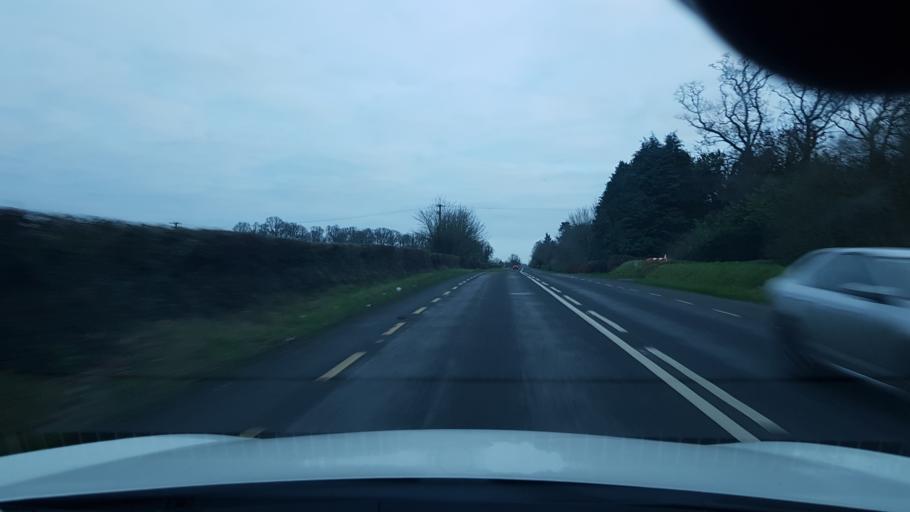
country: IE
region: Leinster
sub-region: An Mhi
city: Navan
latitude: 53.6119
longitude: -6.6317
